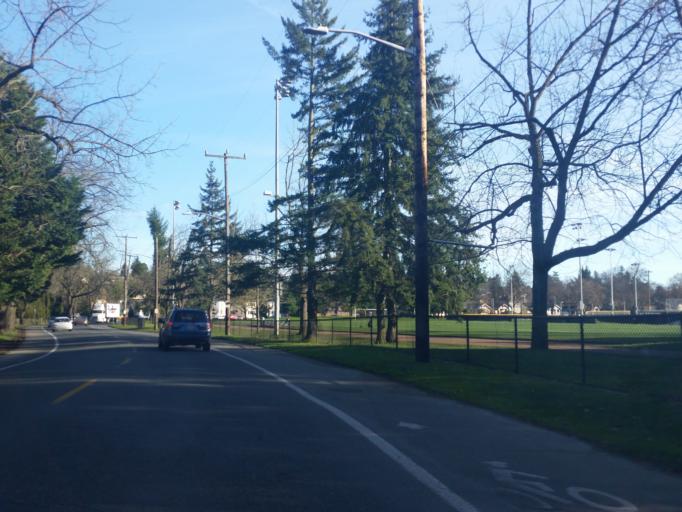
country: US
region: Washington
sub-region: King County
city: Seattle
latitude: 47.6704
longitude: -122.3426
